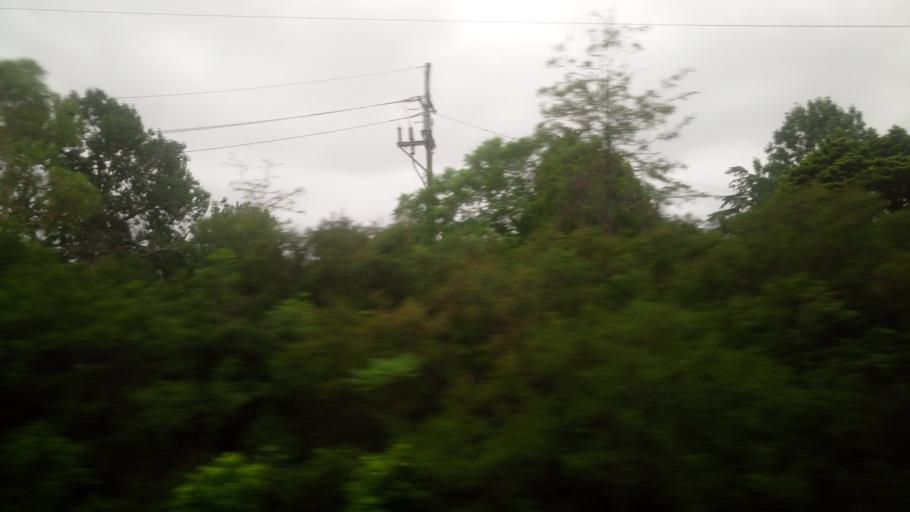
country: AU
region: New South Wales
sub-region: Blue Mountains Municipality
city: Blaxland
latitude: -33.7459
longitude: 150.6158
